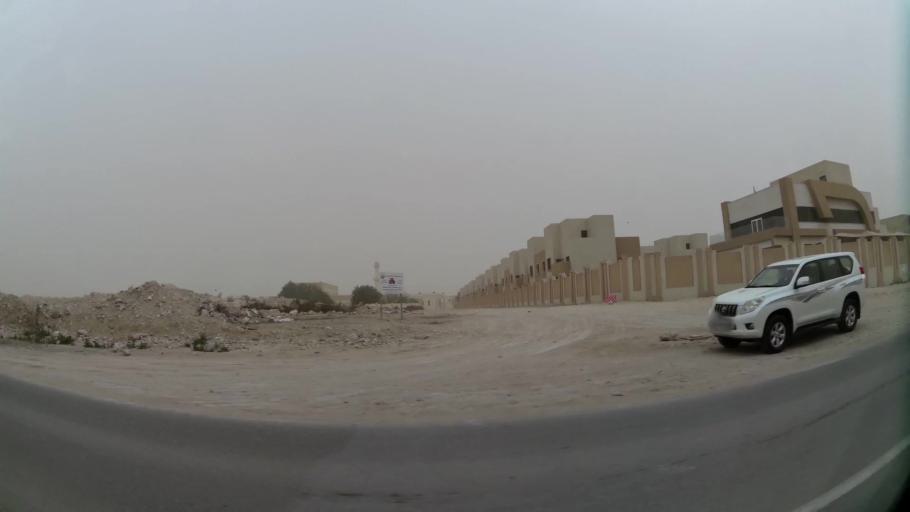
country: QA
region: Baladiyat ad Dawhah
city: Doha
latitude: 25.2422
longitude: 51.4877
